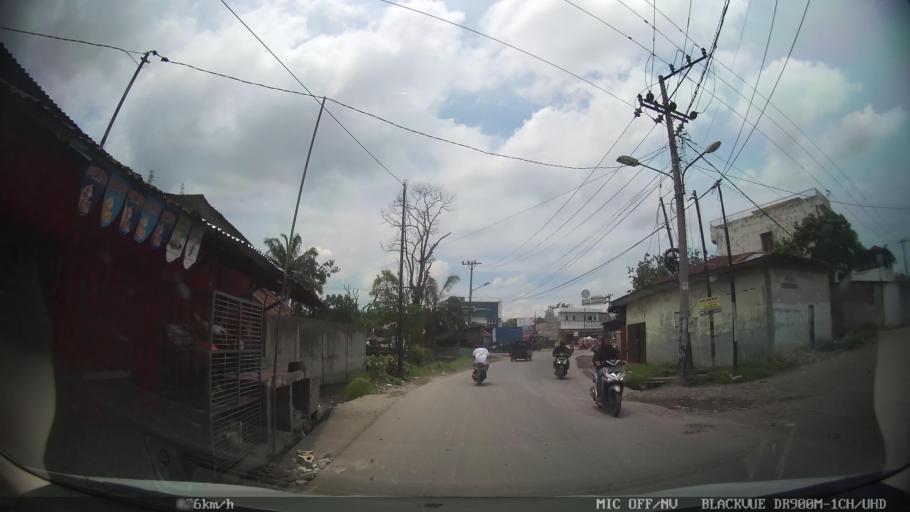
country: ID
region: North Sumatra
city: Labuhan Deli
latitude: 3.6846
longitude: 98.6673
